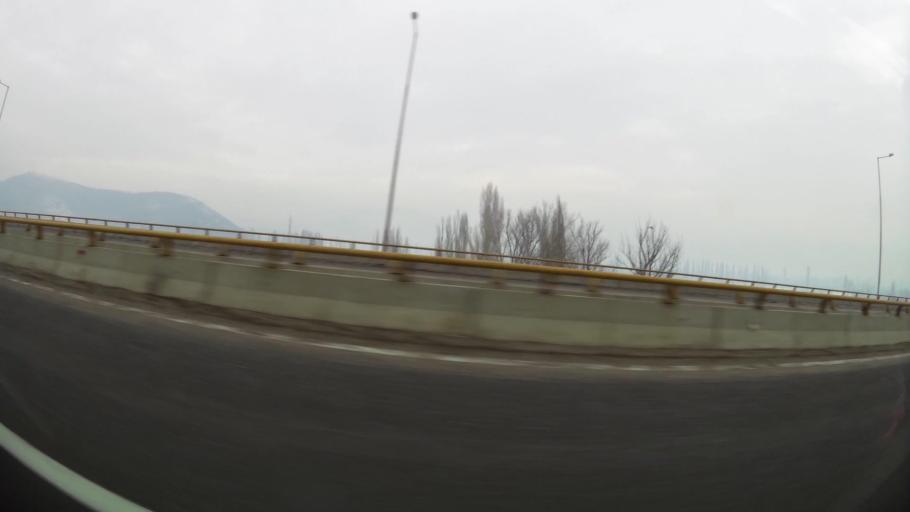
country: MK
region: Cucer-Sandevo
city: Chucher - Sandevo
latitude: 42.0559
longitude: 21.3534
